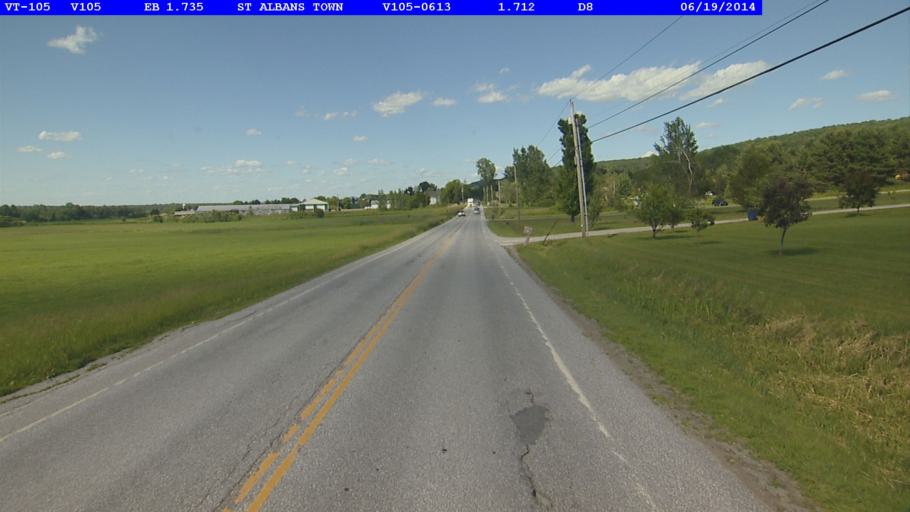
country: US
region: Vermont
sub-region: Franklin County
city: Saint Albans
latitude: 44.8322
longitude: -73.0506
